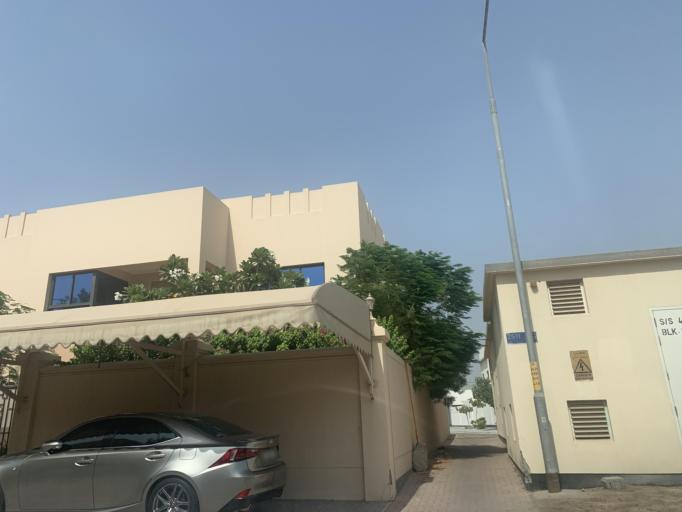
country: BH
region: Manama
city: Jidd Hafs
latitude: 26.2008
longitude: 50.5031
